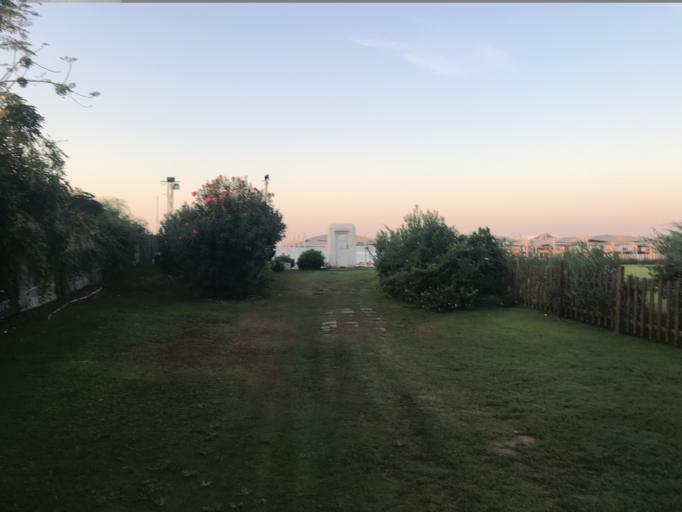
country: TR
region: Antalya
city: Belek
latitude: 36.8576
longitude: 31.0121
